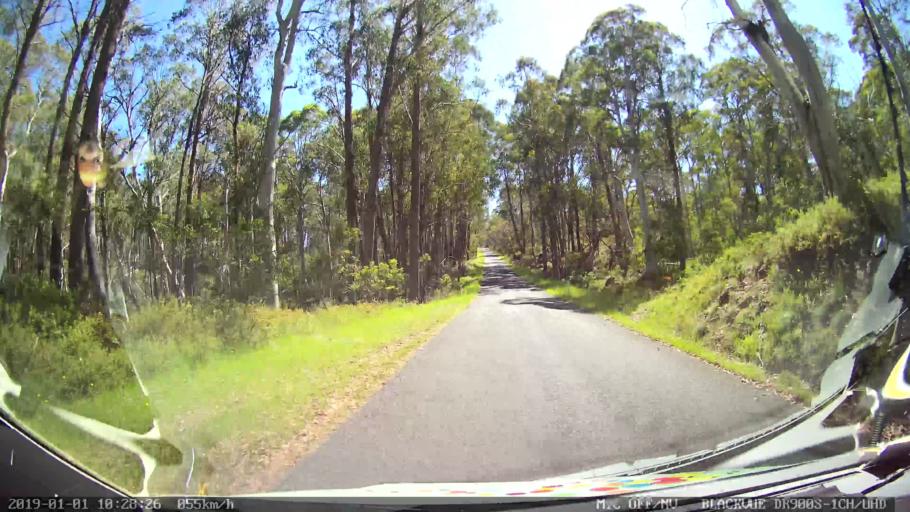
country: AU
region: New South Wales
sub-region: Snowy River
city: Jindabyne
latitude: -36.0602
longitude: 148.2404
